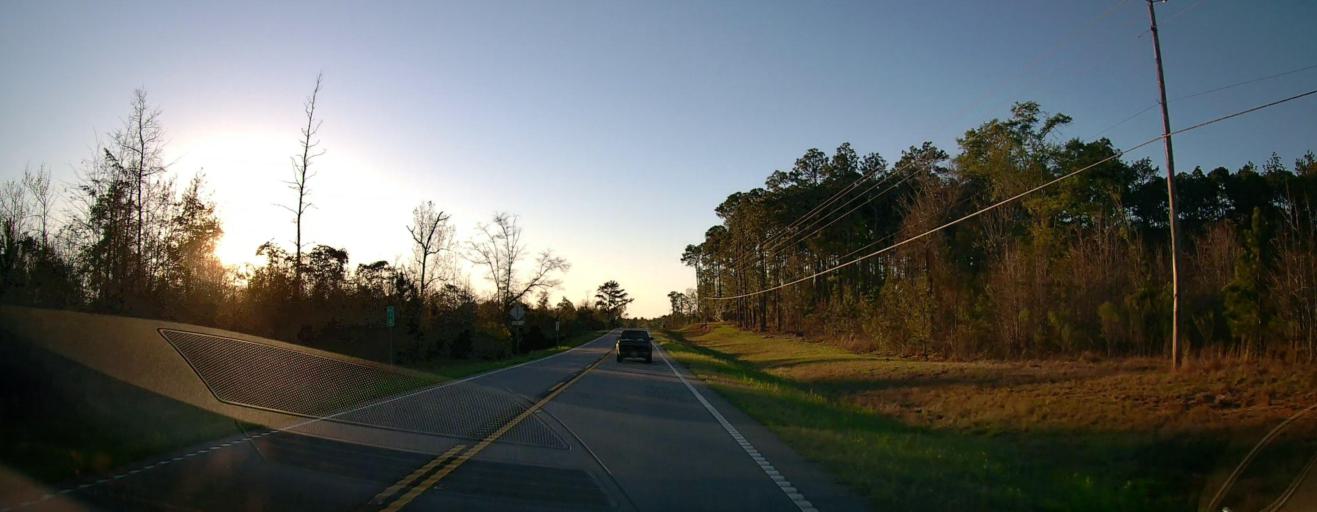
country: US
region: Georgia
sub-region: Crisp County
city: Cordele
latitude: 31.9527
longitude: -83.7202
